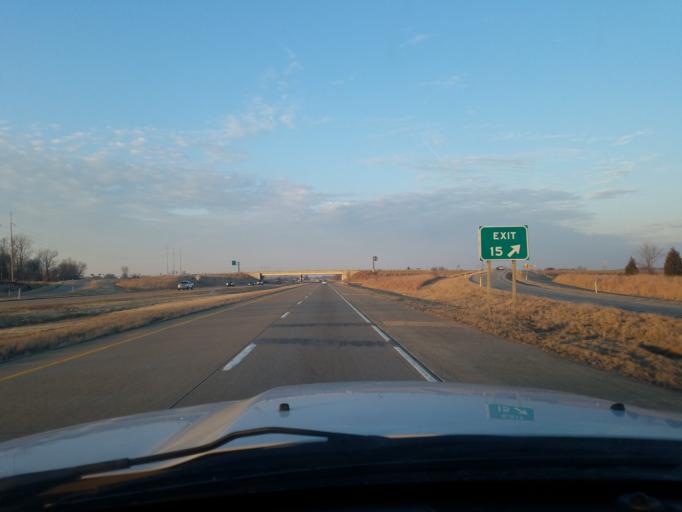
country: US
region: Indiana
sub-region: Vanderburgh County
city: Melody Hill
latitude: 38.0864
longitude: -87.4766
